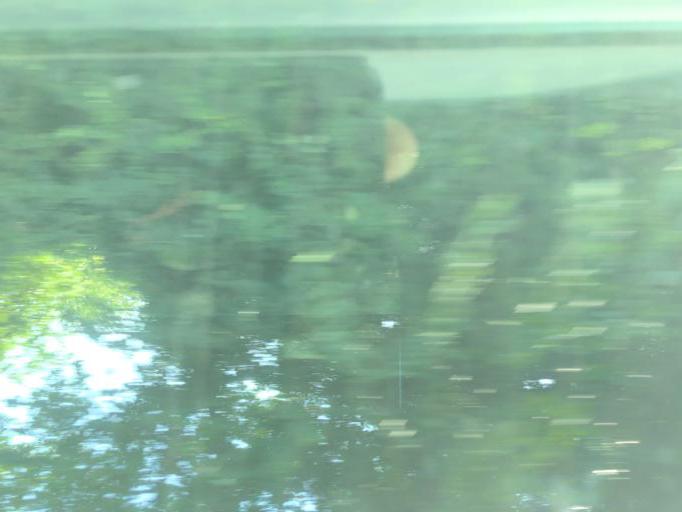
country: IT
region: Emilia-Romagna
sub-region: Provincia di Rimini
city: Rimini
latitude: 44.0708
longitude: 12.5489
